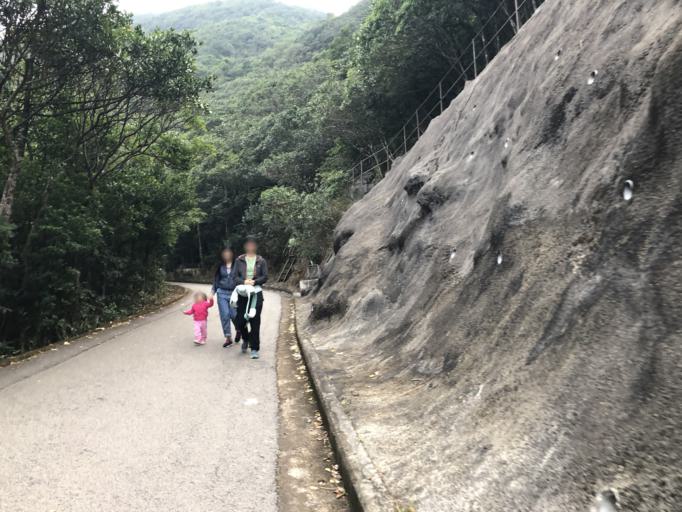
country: HK
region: Wanchai
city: Wan Chai
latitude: 22.2704
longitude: 114.2110
